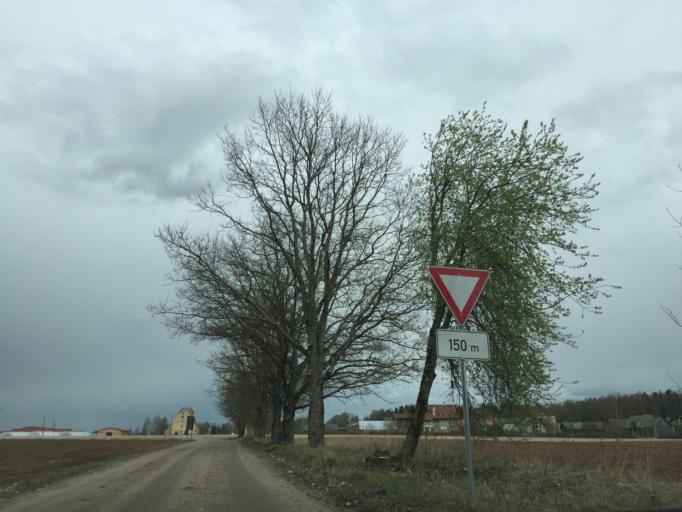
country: LV
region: Priekuli
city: Priekuli
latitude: 57.3092
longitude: 25.3395
